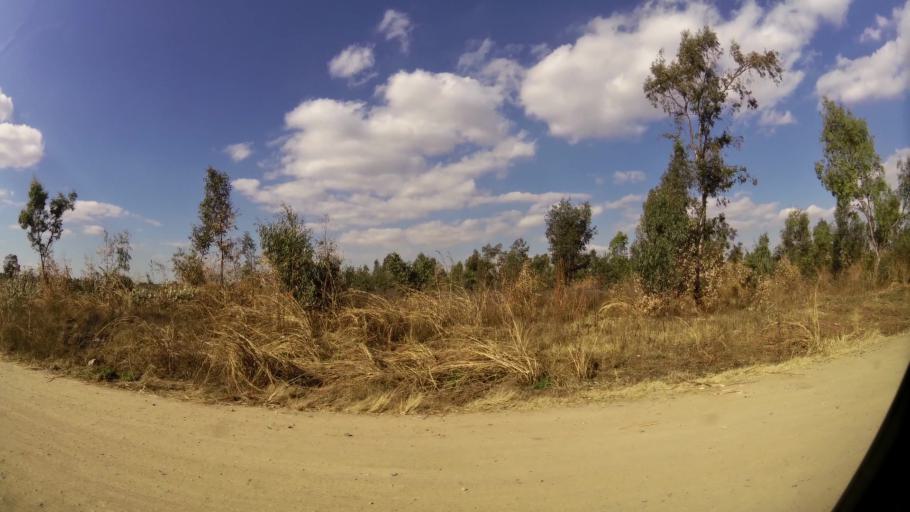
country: ZA
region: Gauteng
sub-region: Ekurhuleni Metropolitan Municipality
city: Tembisa
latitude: -25.9757
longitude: 28.2445
